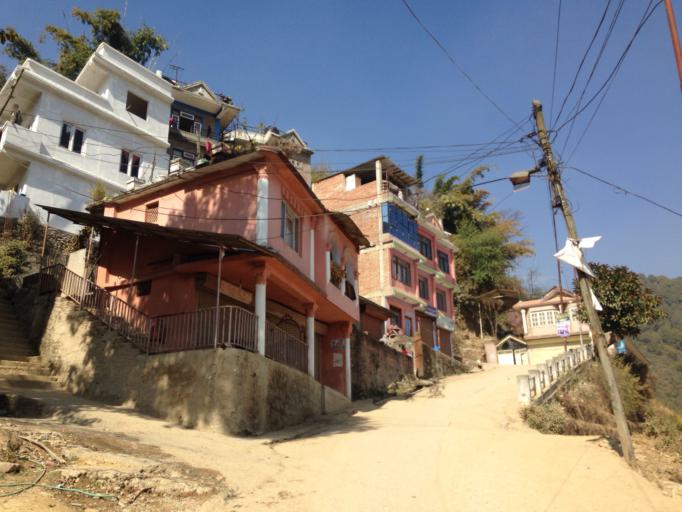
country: NP
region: Central Region
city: Kirtipur
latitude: 27.7237
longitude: 85.2748
